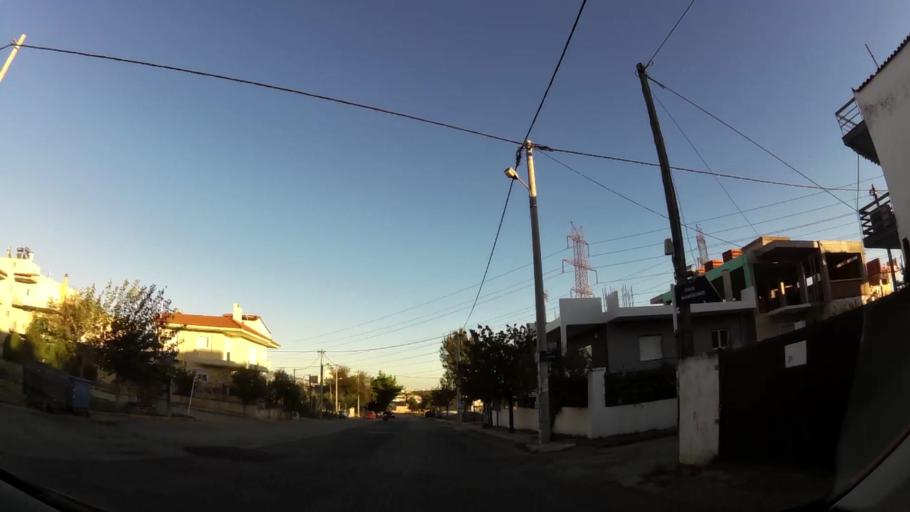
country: GR
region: Attica
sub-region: Nomarchia Dytikis Attikis
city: Ano Liosia
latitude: 38.0923
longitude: 23.7040
